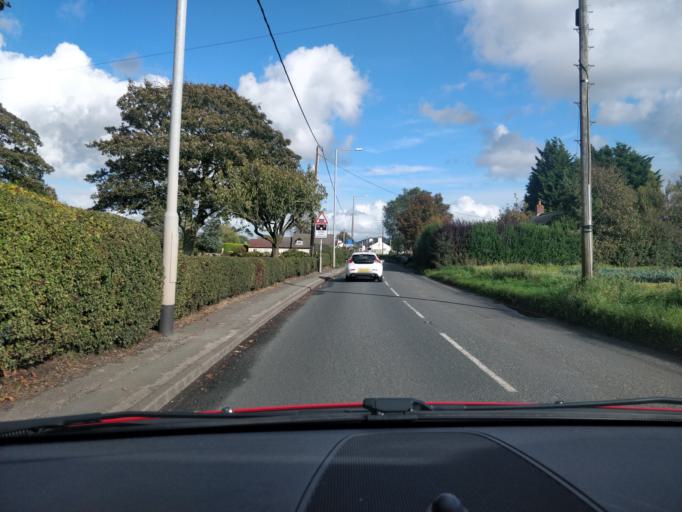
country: GB
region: England
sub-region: Lancashire
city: Parbold
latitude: 53.5972
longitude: -2.8069
